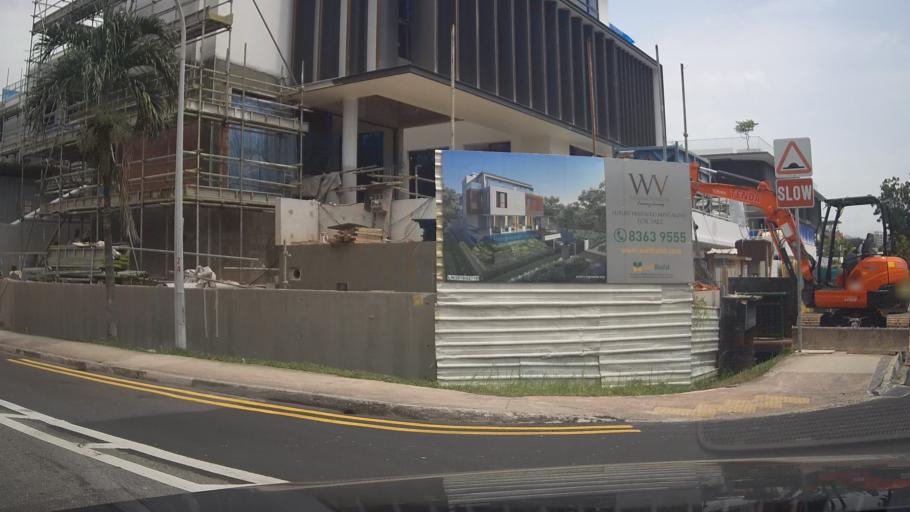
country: SG
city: Singapore
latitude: 1.3029
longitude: 103.8932
